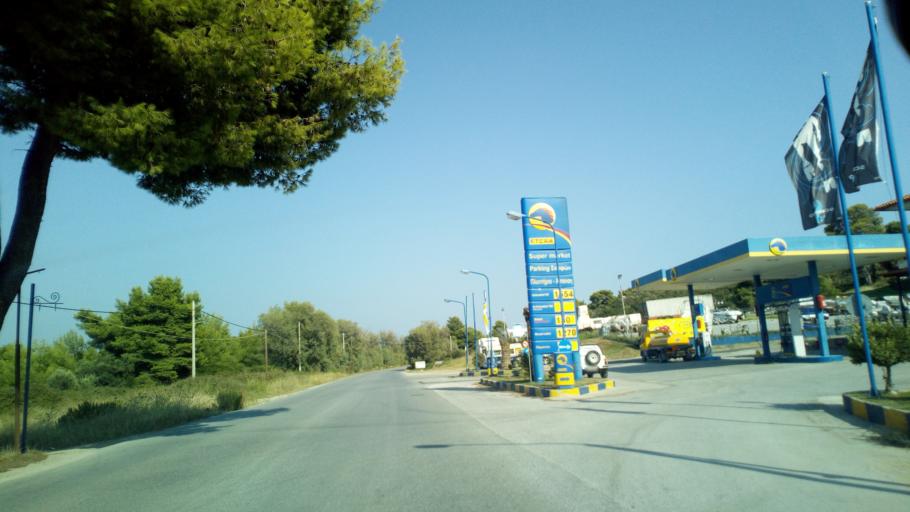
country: GR
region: Central Macedonia
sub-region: Nomos Chalkidikis
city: Pefkochori
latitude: 39.9765
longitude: 23.6597
